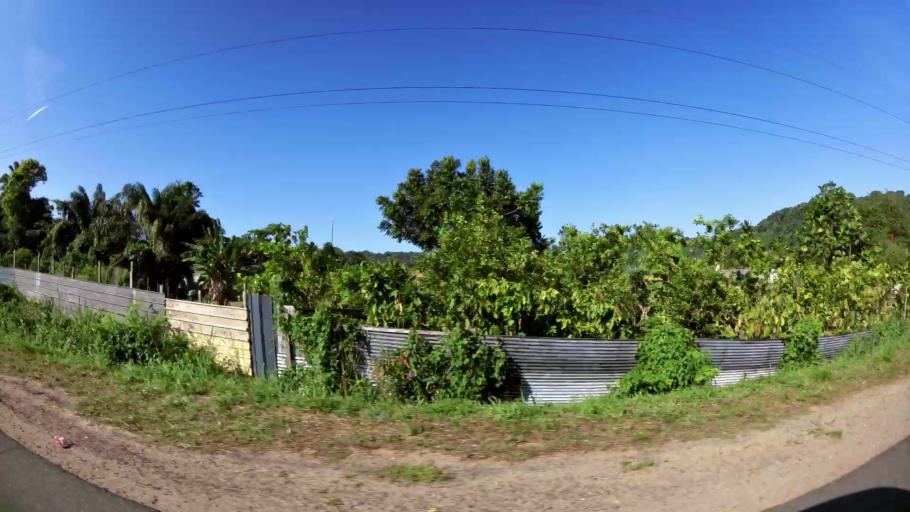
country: GF
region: Guyane
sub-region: Guyane
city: Remire-Montjoly
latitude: 4.8818
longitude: -52.2808
